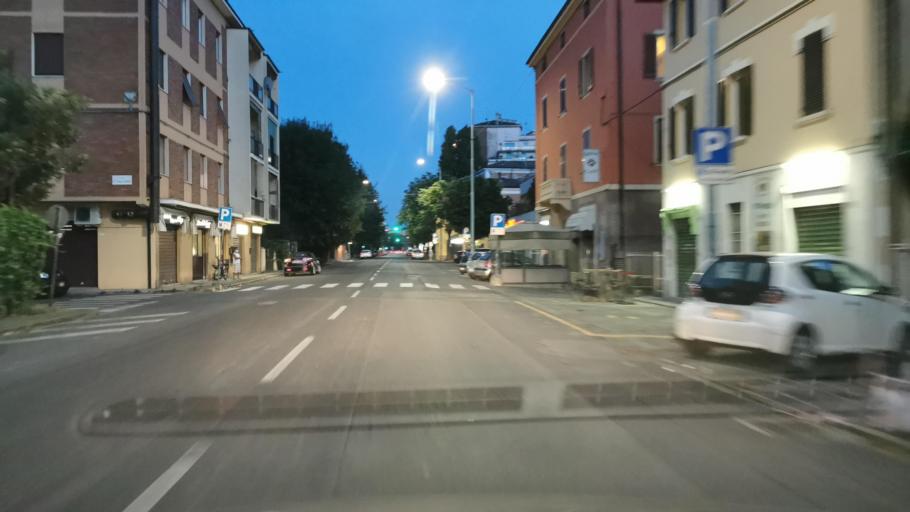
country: IT
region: Emilia-Romagna
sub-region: Provincia di Modena
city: Modena
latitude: 44.6384
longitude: 10.9321
